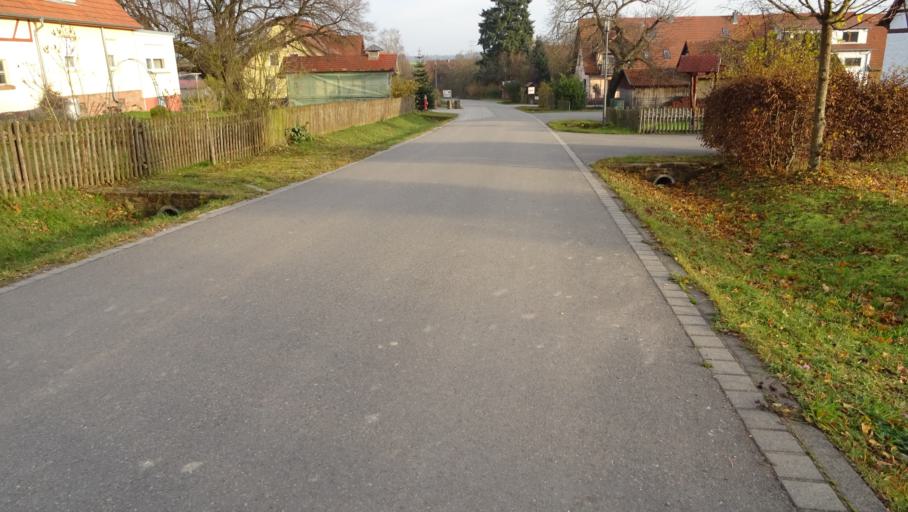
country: DE
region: Baden-Wuerttemberg
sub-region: Karlsruhe Region
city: Neckargerach
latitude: 49.4155
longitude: 9.0716
